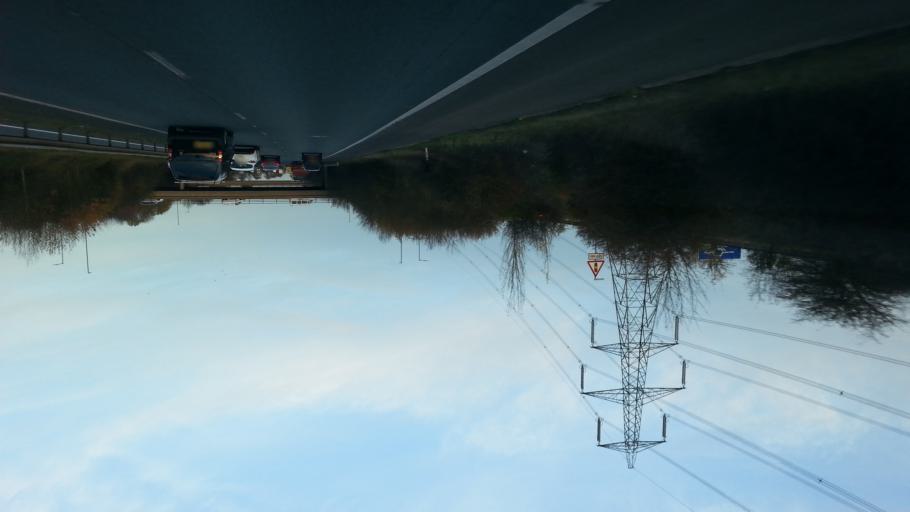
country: GB
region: England
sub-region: Hertfordshire
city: Letchworth Garden City
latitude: 51.9622
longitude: -0.2054
